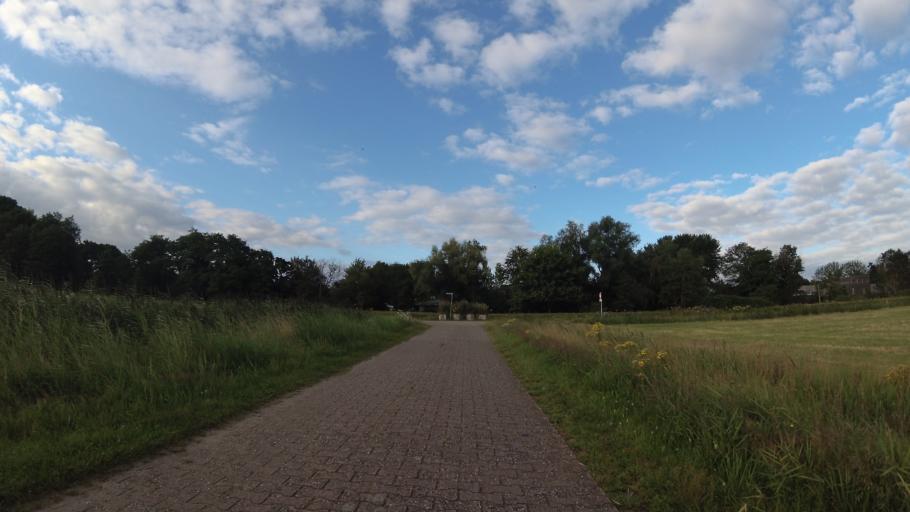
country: NL
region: North Brabant
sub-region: Gemeente Breda
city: Hoge Vucht
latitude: 51.6161
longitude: 4.7877
